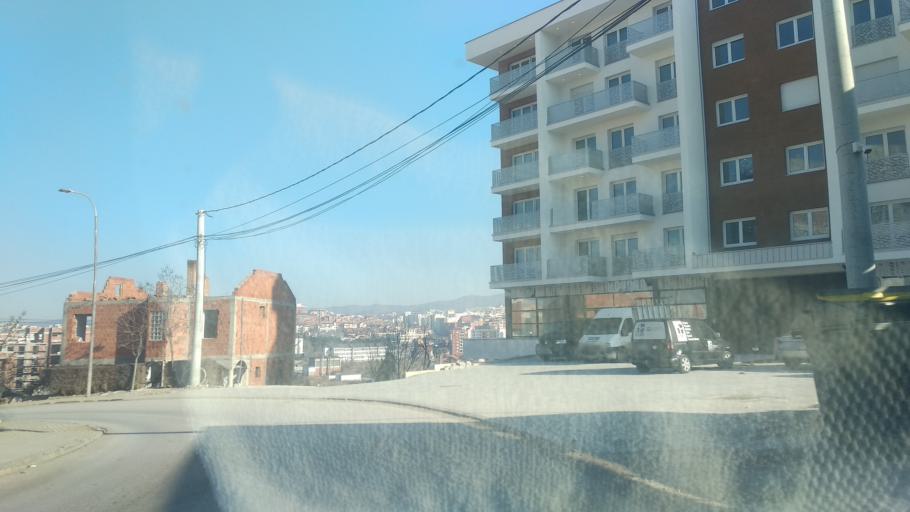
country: XK
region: Pristina
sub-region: Komuna e Prishtines
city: Pristina
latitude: 42.6383
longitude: 21.1603
